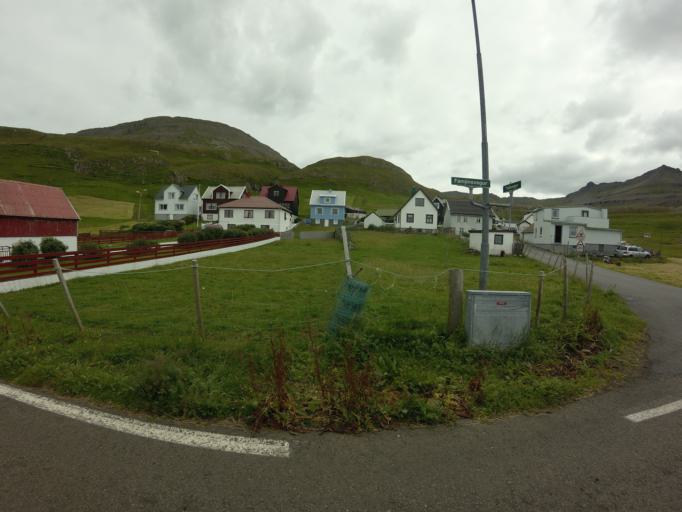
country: FO
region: Suduroy
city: Tvoroyri
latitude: 61.5240
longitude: -6.8794
